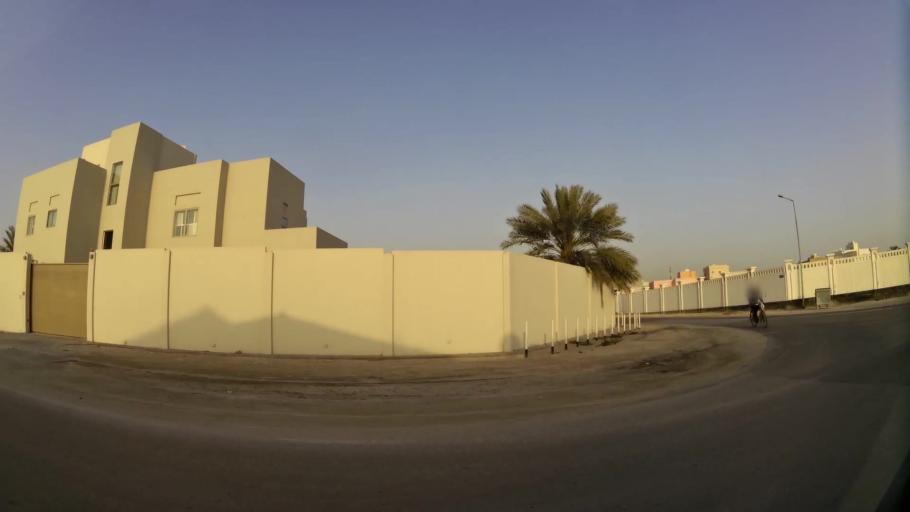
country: BH
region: Northern
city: Madinat `Isa
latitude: 26.1925
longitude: 50.4767
